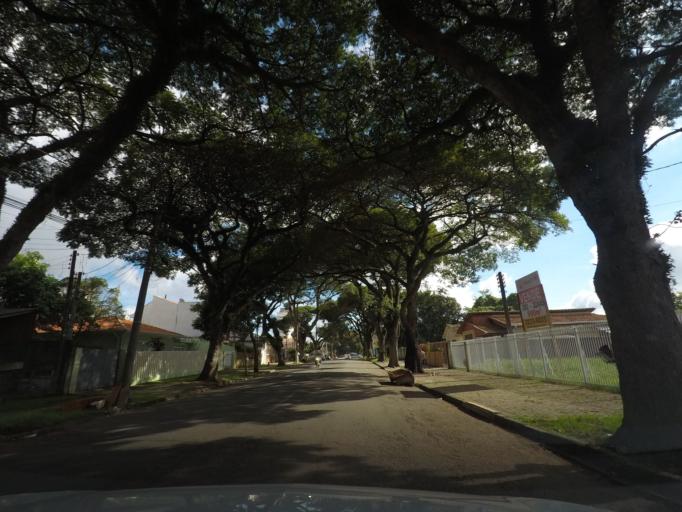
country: BR
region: Parana
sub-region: Curitiba
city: Curitiba
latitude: -25.4468
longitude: -49.2526
